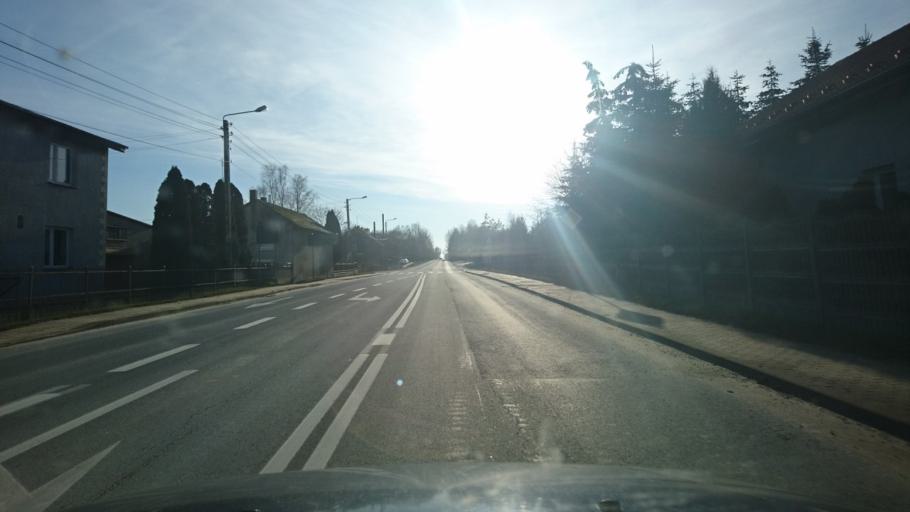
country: PL
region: Opole Voivodeship
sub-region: Powiat oleski
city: Dalachow
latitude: 51.0757
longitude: 18.6026
